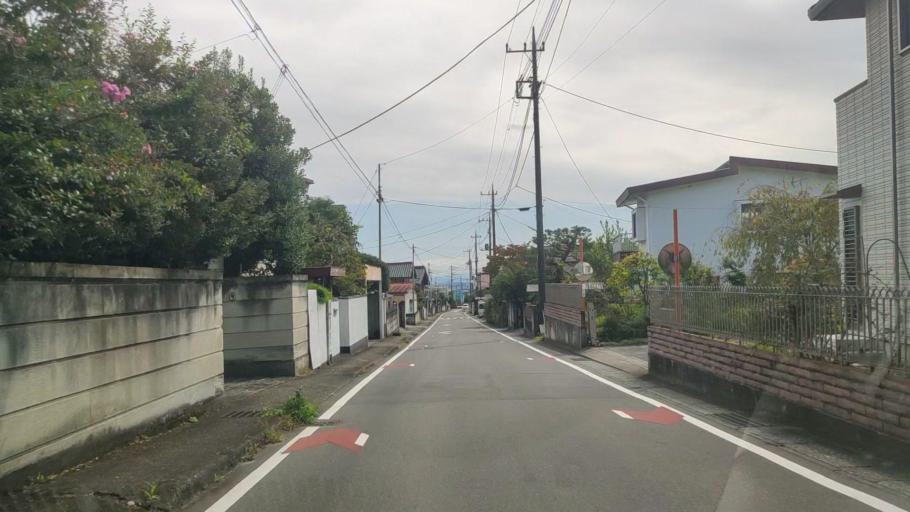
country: JP
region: Gunma
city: Kanekomachi
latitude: 36.3931
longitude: 138.9571
